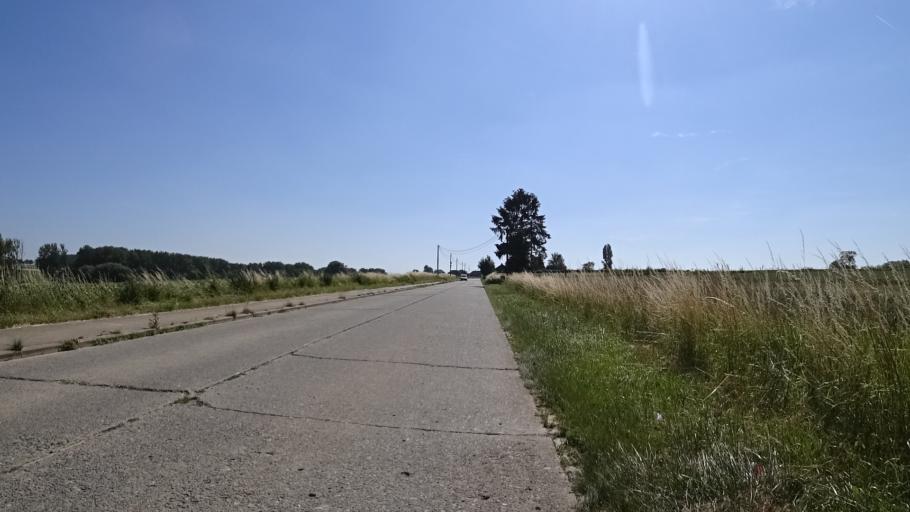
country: BE
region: Wallonia
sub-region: Province du Brabant Wallon
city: Jodoigne
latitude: 50.7159
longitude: 4.8529
